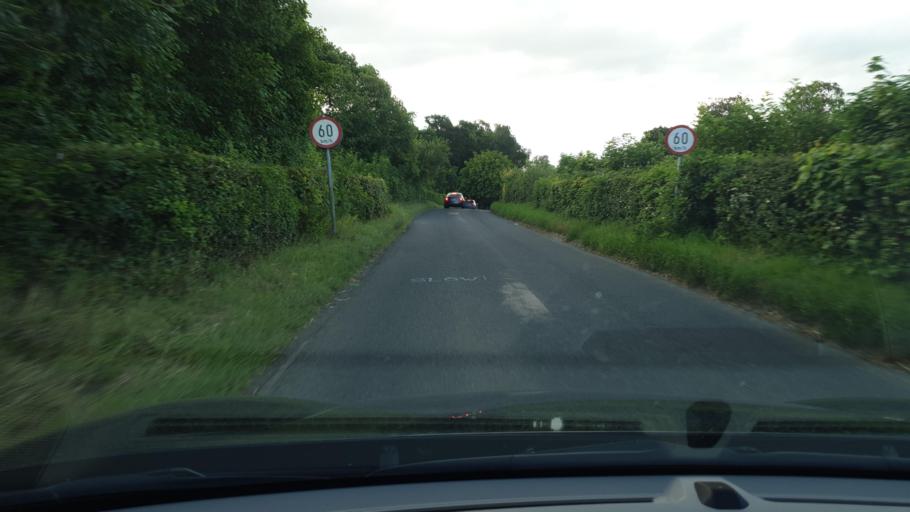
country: IE
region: Leinster
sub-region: Lu
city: Drogheda
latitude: 53.6915
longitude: -6.3423
